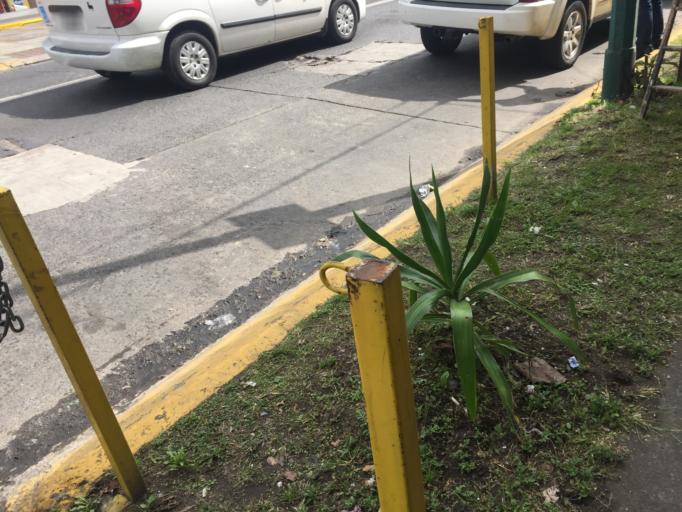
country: MX
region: Veracruz
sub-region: Xalapa
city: Xalapa de Enriquez
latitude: 19.5308
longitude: -96.9136
